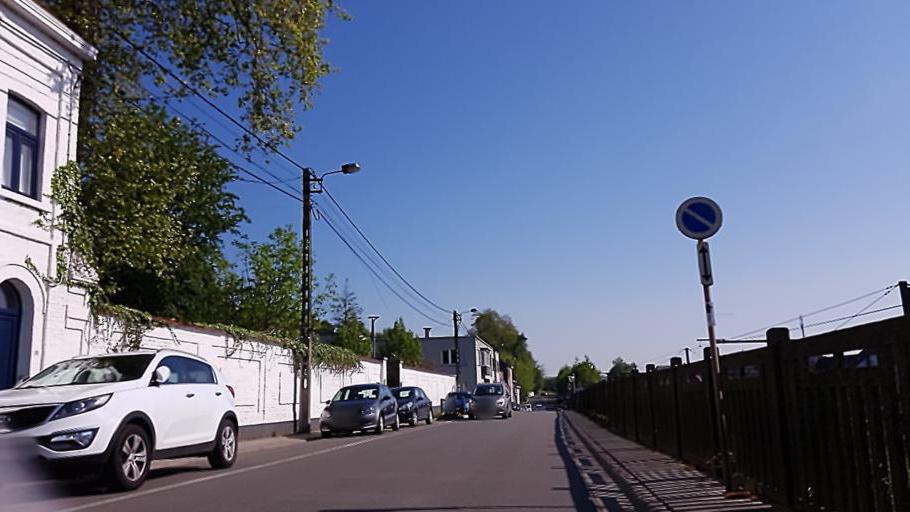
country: BE
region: Wallonia
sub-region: Province du Brabant Wallon
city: Wavre
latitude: 50.7159
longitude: 4.6044
